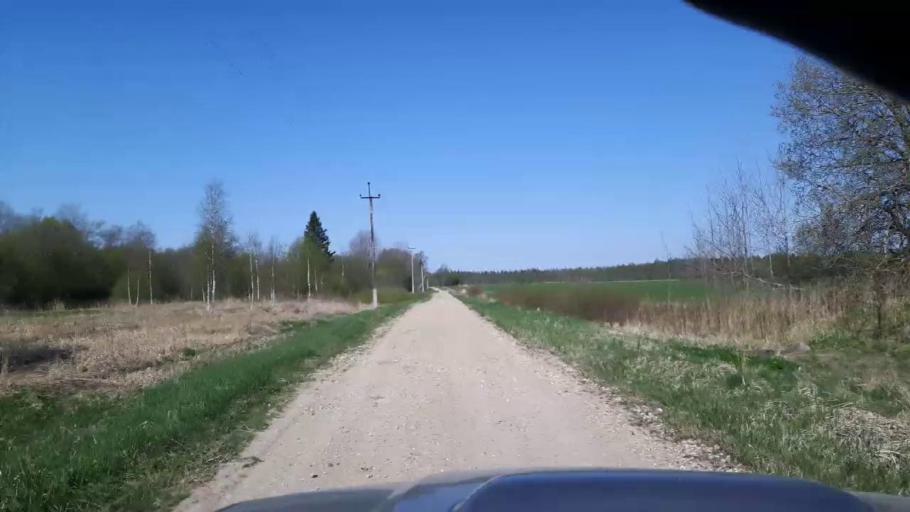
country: EE
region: Paernumaa
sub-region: Tootsi vald
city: Tootsi
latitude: 58.4450
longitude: 24.8110
